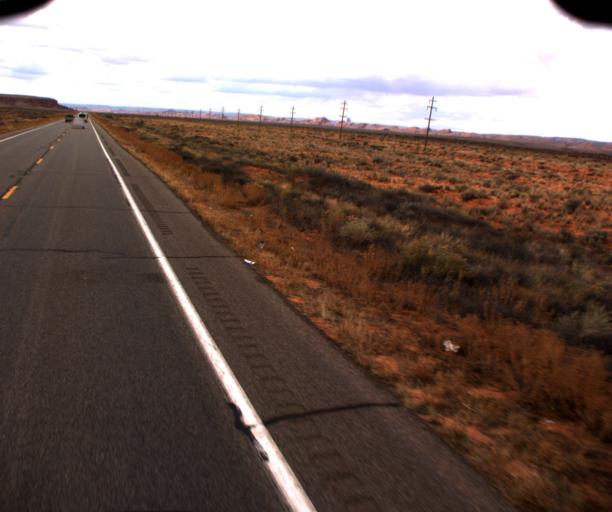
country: US
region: Arizona
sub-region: Navajo County
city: Kayenta
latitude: 36.7865
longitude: -109.9593
